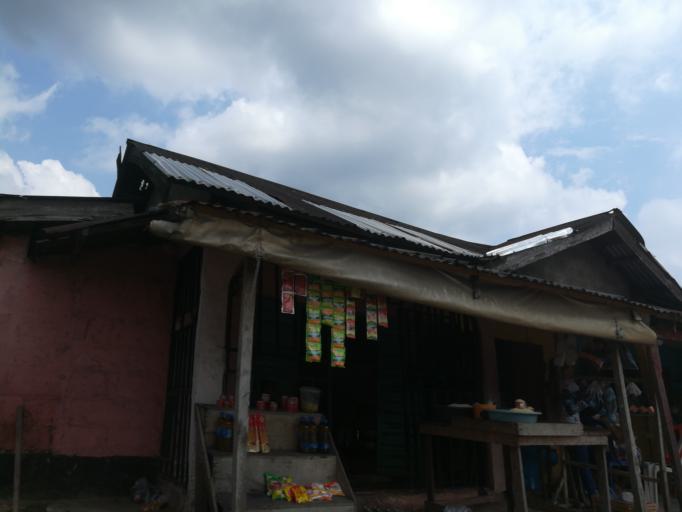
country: NG
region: Rivers
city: Okrika
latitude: 4.7253
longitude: 7.1529
